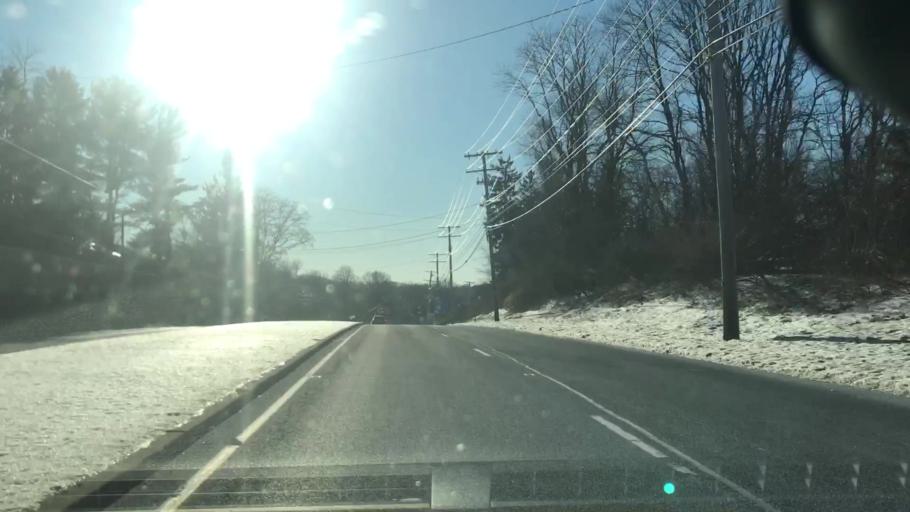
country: US
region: New Jersey
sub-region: Morris County
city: Chester
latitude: 40.7855
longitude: -74.6997
